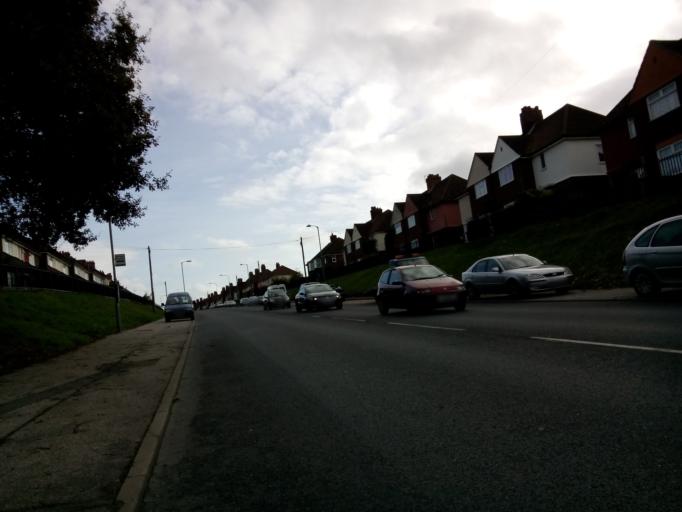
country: GB
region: England
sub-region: Suffolk
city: Ipswich
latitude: 52.0380
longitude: 1.1717
